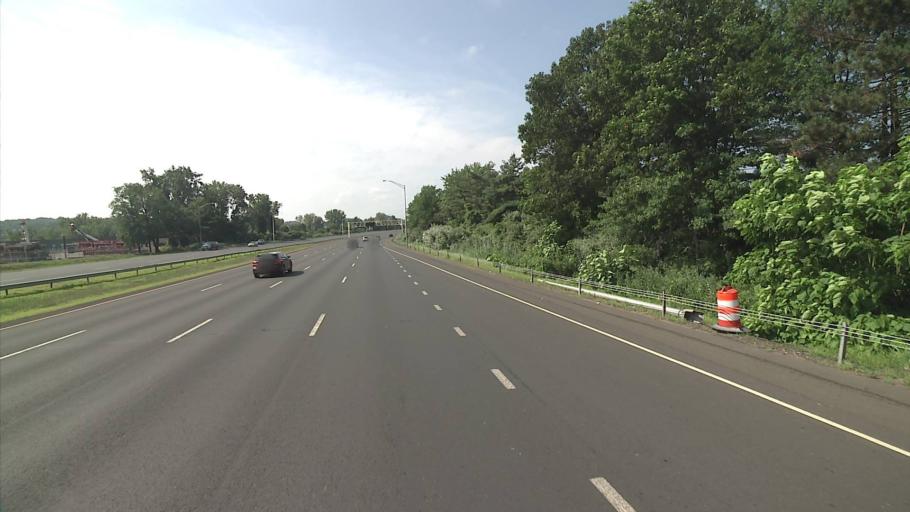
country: US
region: Connecticut
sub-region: New Haven County
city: North Haven
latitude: 41.3458
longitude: -72.8688
